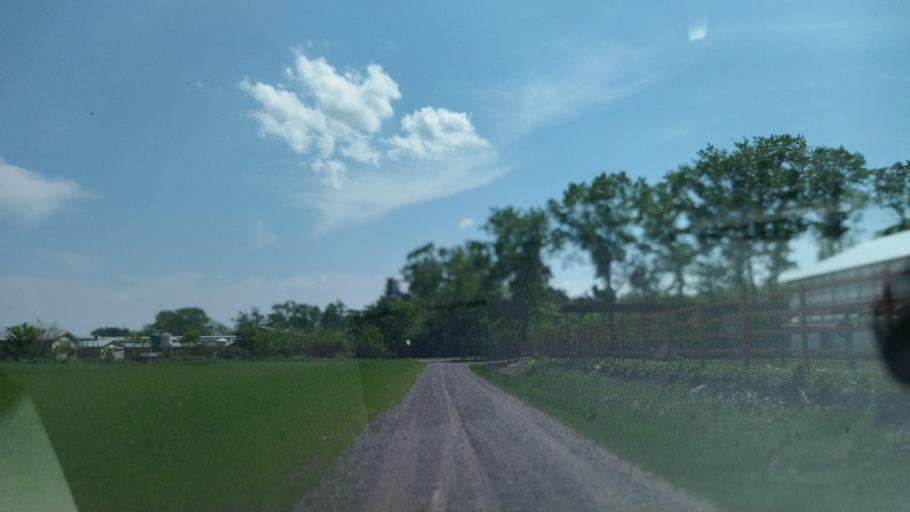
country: JP
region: Hokkaido
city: Otofuke
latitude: 43.1331
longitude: 143.2181
